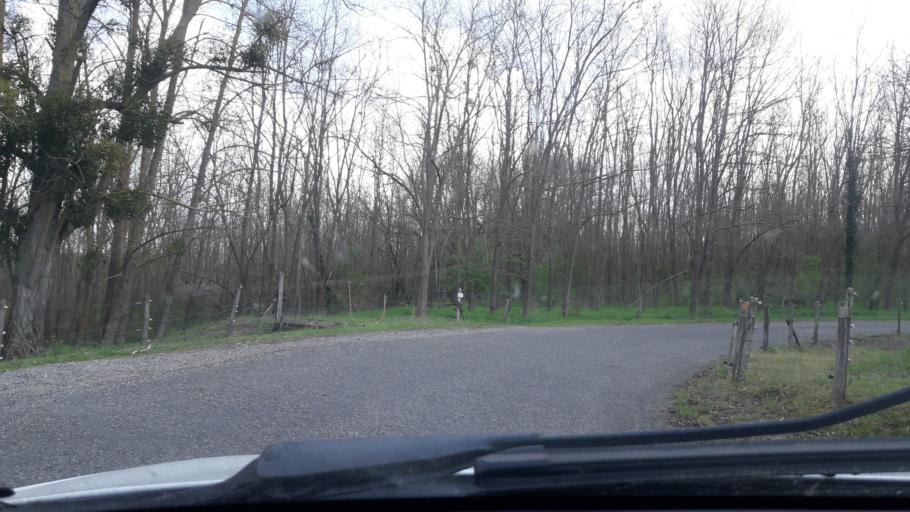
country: FR
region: Midi-Pyrenees
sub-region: Departement de la Haute-Garonne
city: Montesquieu-Volvestre
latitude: 43.2172
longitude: 1.2271
